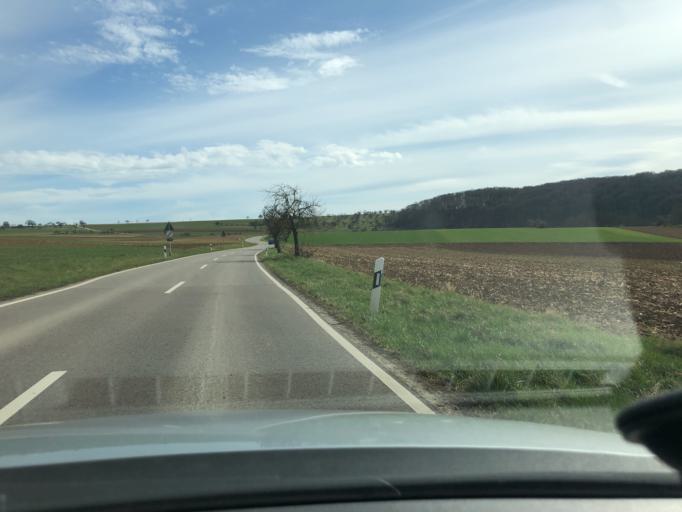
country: DE
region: Baden-Wuerttemberg
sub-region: Karlsruhe Region
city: Illingen
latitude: 48.9314
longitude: 8.9220
